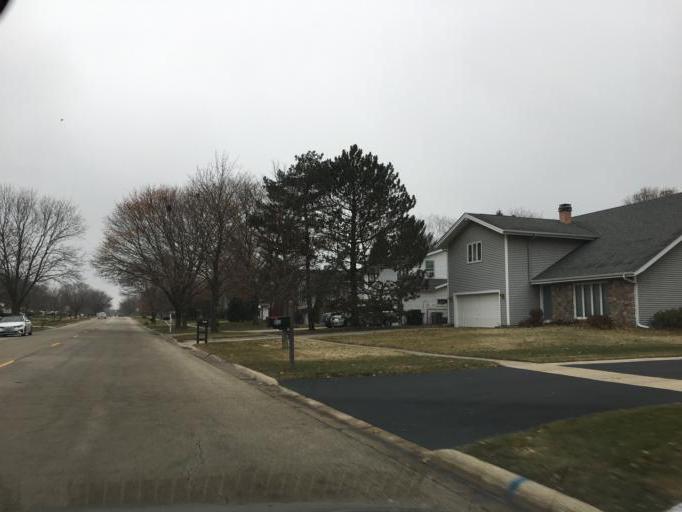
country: US
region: Illinois
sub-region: McHenry County
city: Lakewood
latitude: 42.2169
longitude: -88.3583
